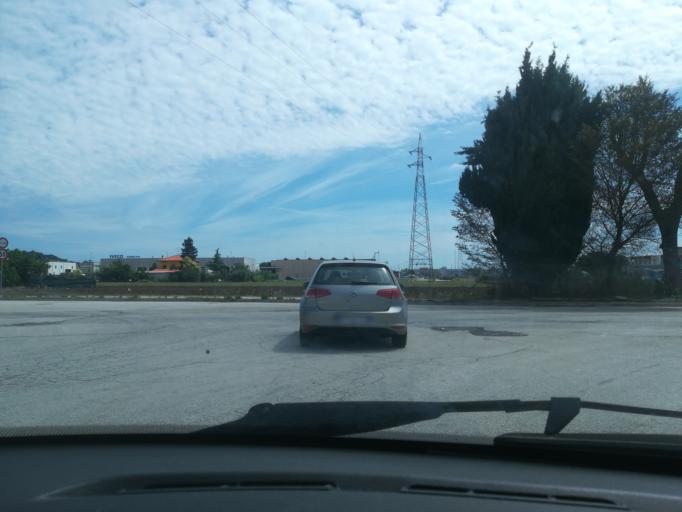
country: IT
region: The Marches
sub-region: Provincia di Macerata
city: Santa Maria Apparente
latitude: 43.2842
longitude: 13.6808
